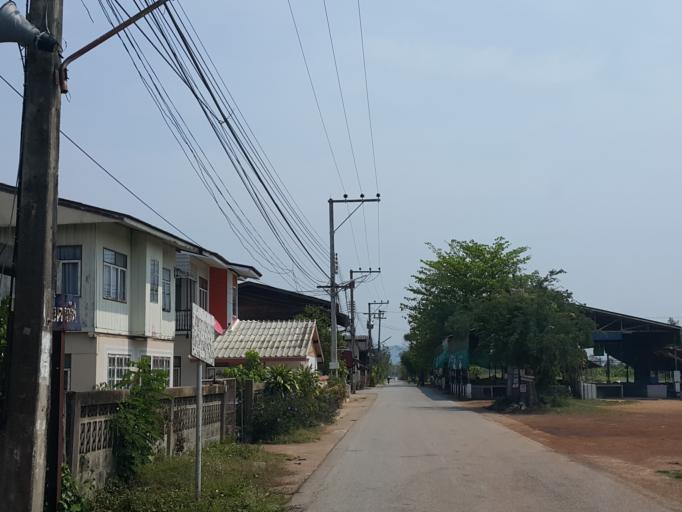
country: TH
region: Lampang
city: Lampang
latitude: 18.3020
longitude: 99.4325
